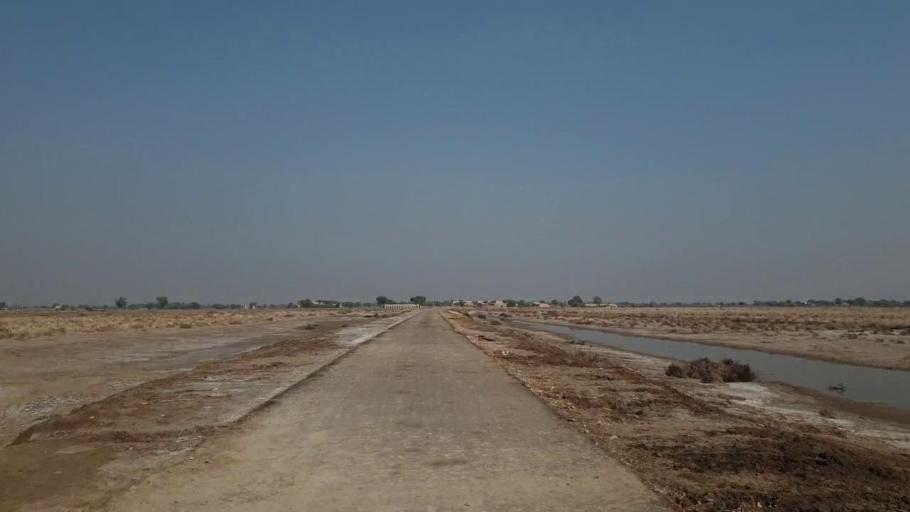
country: PK
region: Sindh
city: Sehwan
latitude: 26.4286
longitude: 67.7708
